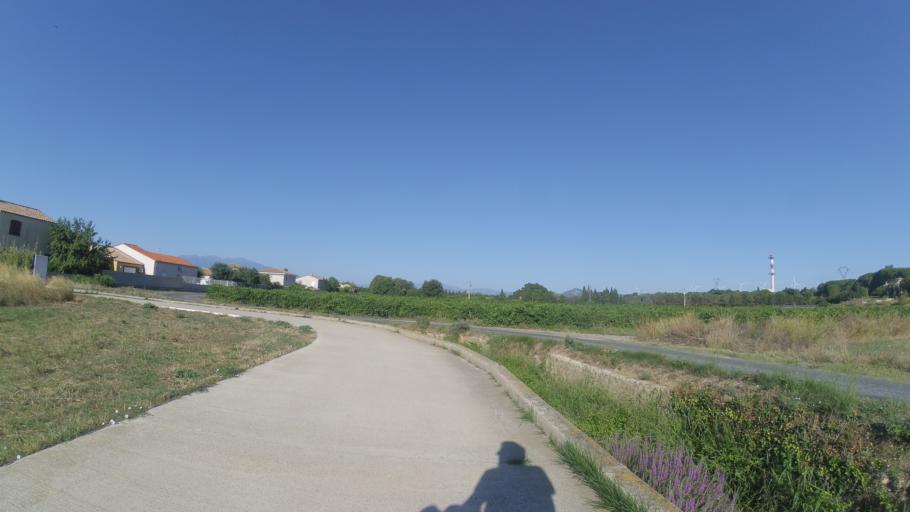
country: FR
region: Languedoc-Roussillon
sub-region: Departement des Pyrenees-Orientales
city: Baho
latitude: 42.7062
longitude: 2.8198
